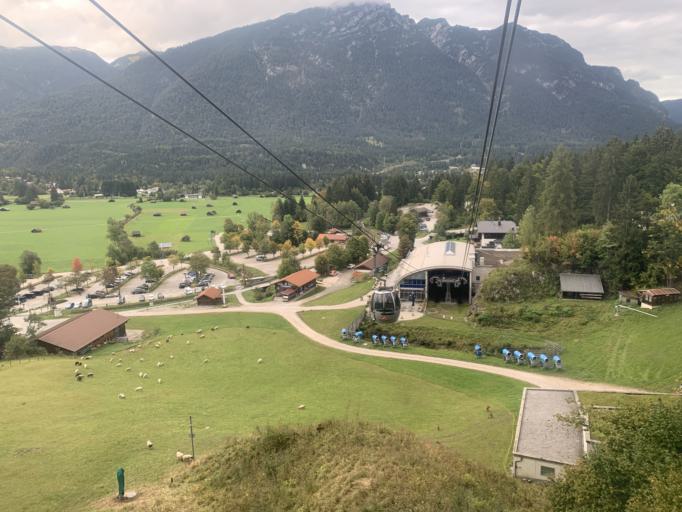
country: DE
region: Bavaria
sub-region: Upper Bavaria
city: Garmisch-Partenkirchen
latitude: 47.4701
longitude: 11.0640
